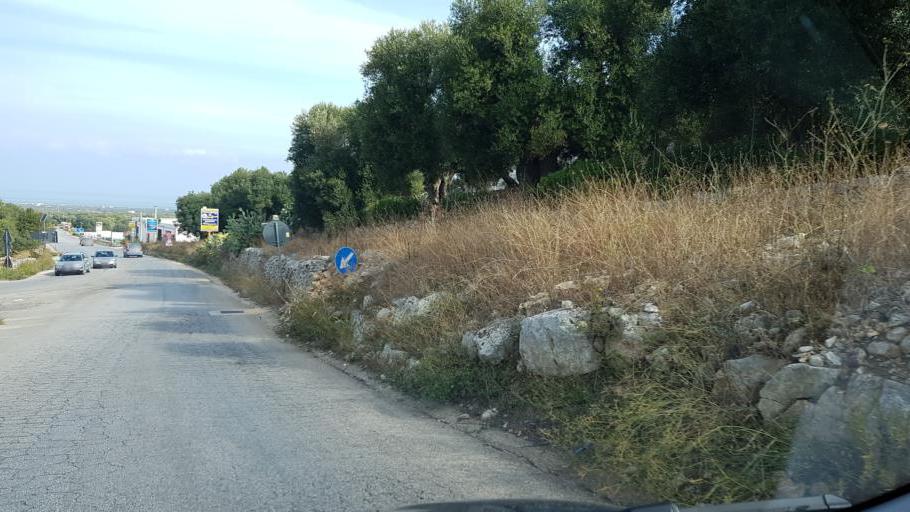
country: IT
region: Apulia
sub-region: Provincia di Brindisi
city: Ostuni
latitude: 40.7400
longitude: 17.5775
